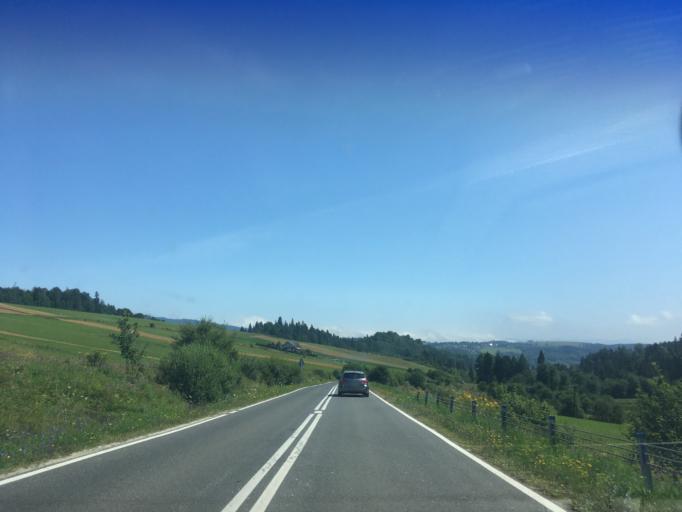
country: PL
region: Lesser Poland Voivodeship
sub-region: Powiat nowotarski
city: Niedzica
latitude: 49.4255
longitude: 20.2785
